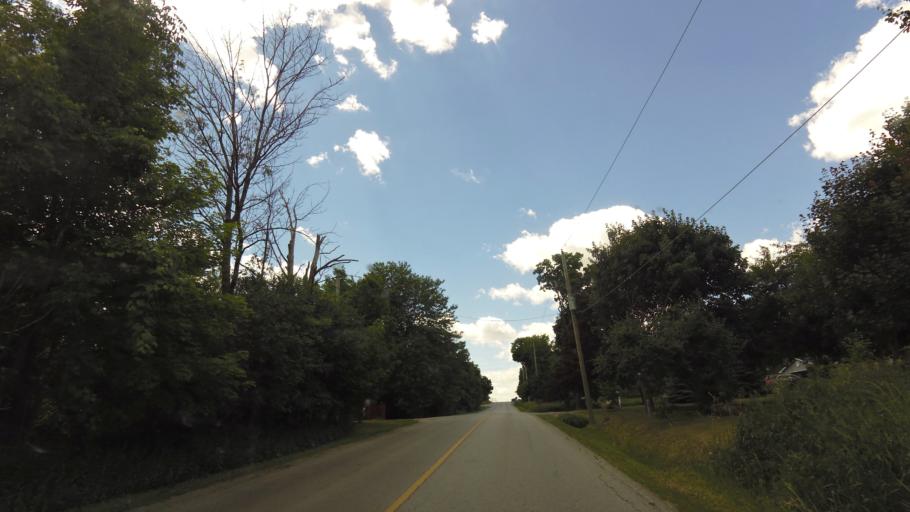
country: CA
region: Ontario
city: Oshawa
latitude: 43.9618
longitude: -78.8355
